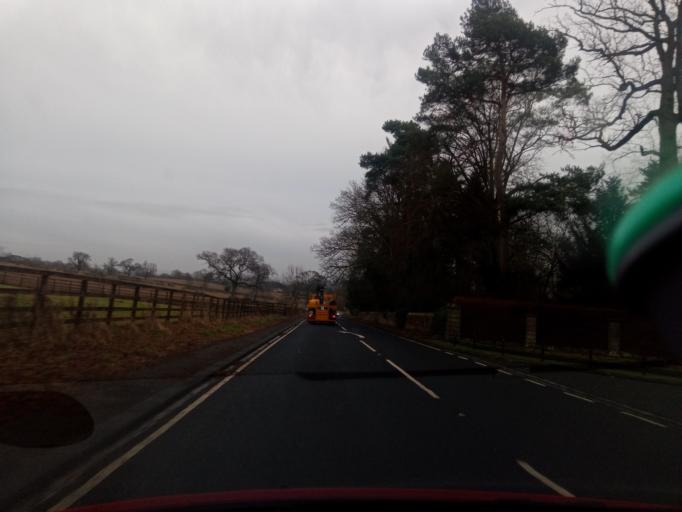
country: GB
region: England
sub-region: Northumberland
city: Wall
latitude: 55.0288
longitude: -2.1407
